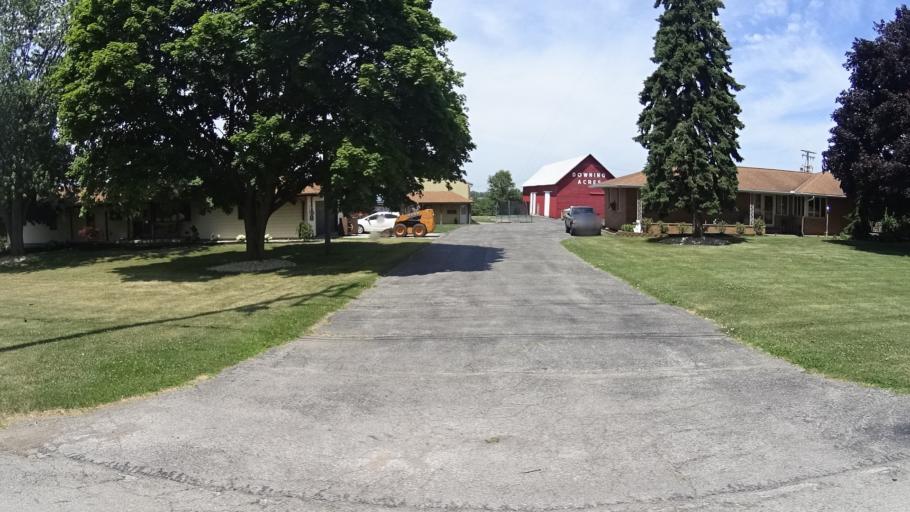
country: US
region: Ohio
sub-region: Erie County
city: Sandusky
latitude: 41.4042
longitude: -82.7849
